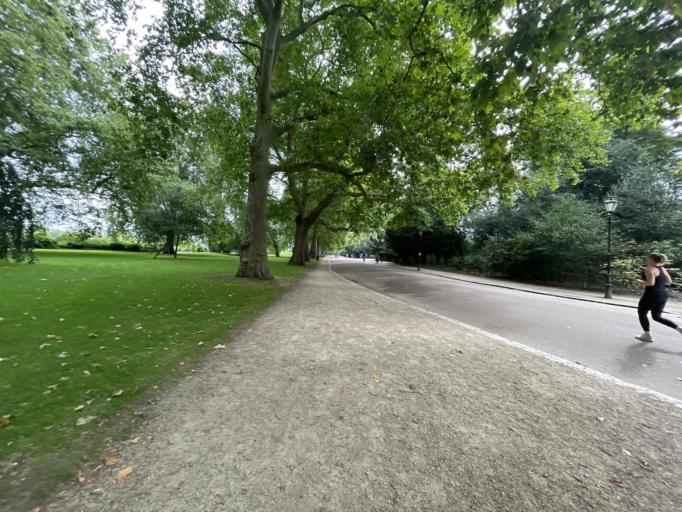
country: GB
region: England
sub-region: Greater London
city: Battersea
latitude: 51.4812
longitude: -0.1623
